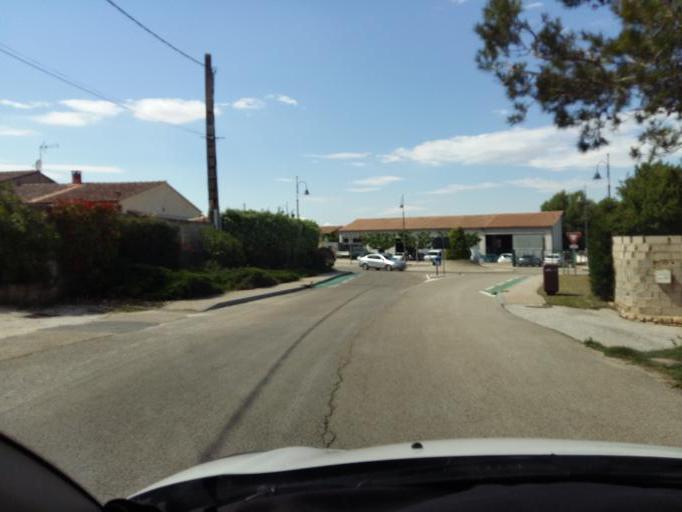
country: FR
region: Provence-Alpes-Cote d'Azur
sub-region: Departement du Vaucluse
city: Robion
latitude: 43.8494
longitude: 5.1218
